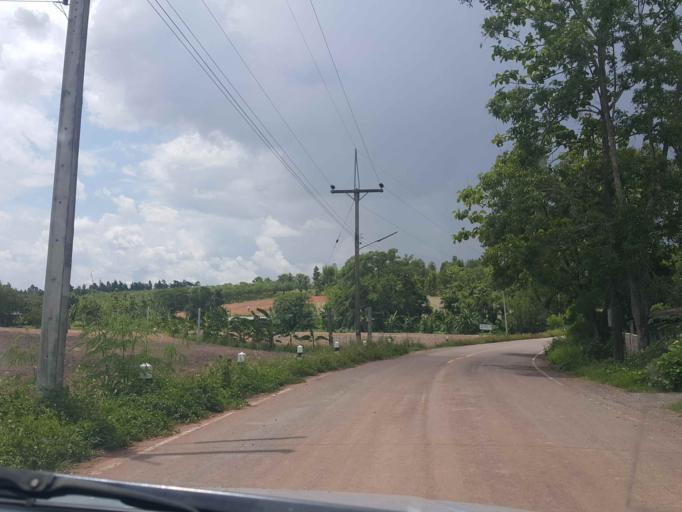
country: TH
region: Phayao
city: Dok Kham Tai
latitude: 19.0508
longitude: 99.9494
